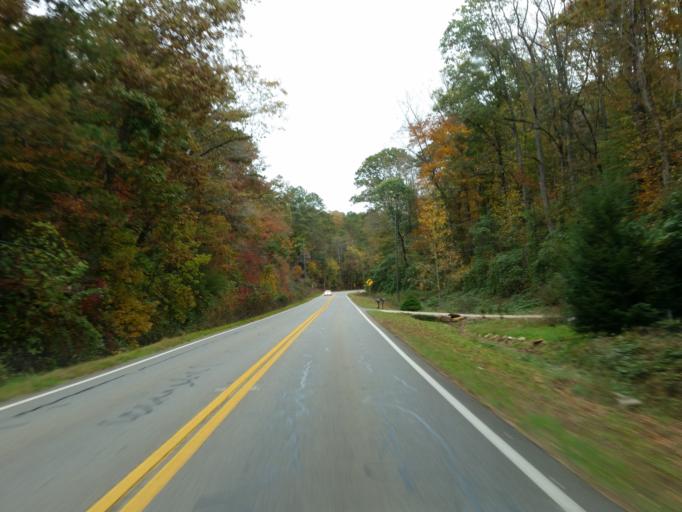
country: US
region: Georgia
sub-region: Pickens County
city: Jasper
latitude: 34.5162
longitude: -84.4276
